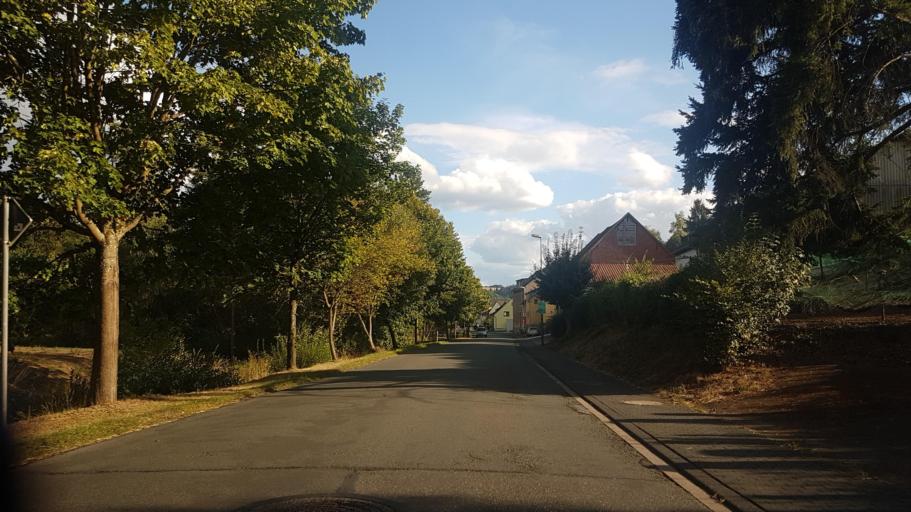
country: DE
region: Rheinland-Pfalz
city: Hoppstadten-Weiersbach
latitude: 49.6230
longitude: 7.1951
